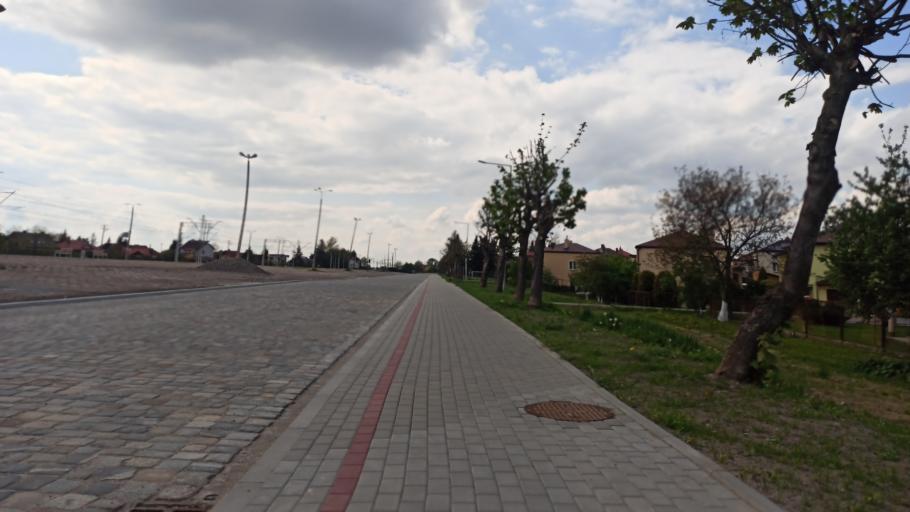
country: PL
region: Subcarpathian Voivodeship
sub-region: Powiat jaroslawski
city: Radymno
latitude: 49.9401
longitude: 22.8287
